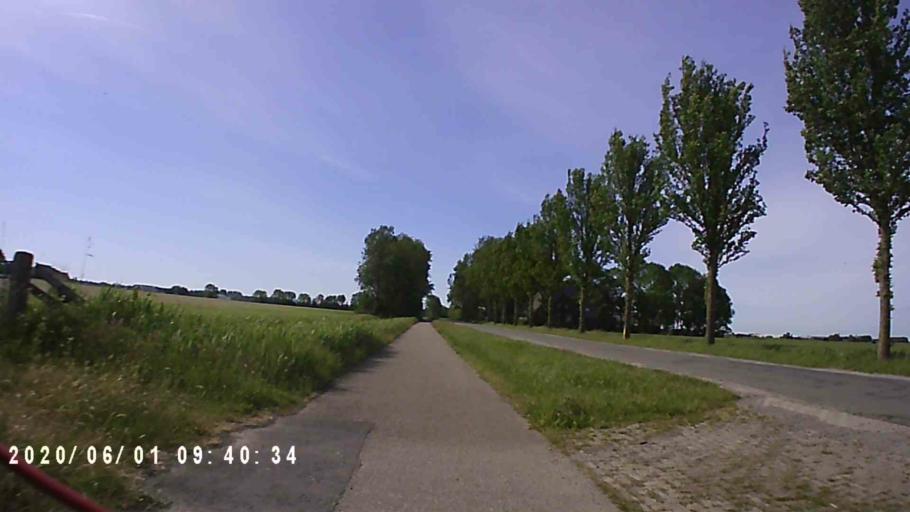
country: NL
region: Friesland
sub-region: Menameradiel
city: Berltsum
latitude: 53.2515
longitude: 5.6815
